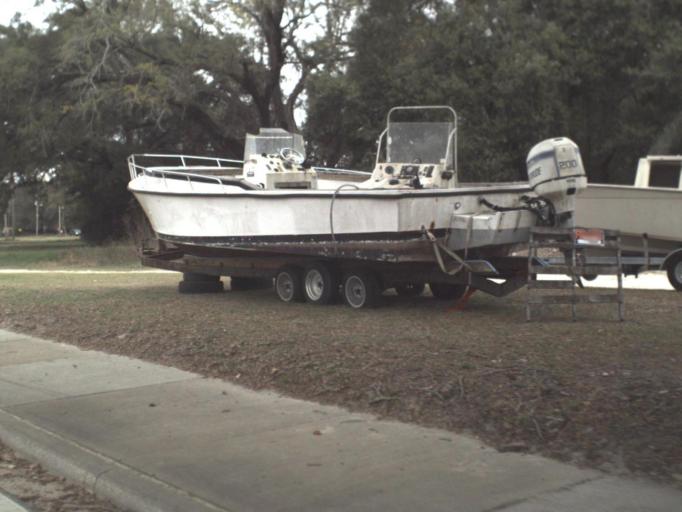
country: US
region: Florida
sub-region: Bay County
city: Springfield
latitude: 30.1459
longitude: -85.6156
